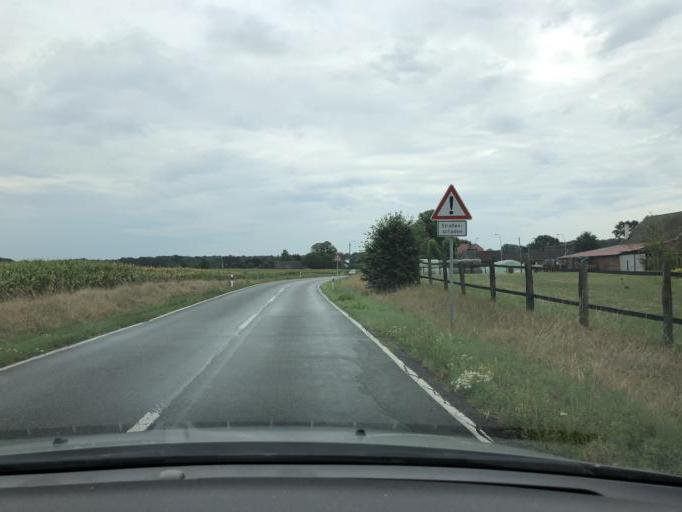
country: DE
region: North Rhine-Westphalia
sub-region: Regierungsbezirk Dusseldorf
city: Schermbeck
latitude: 51.6486
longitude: 6.8932
